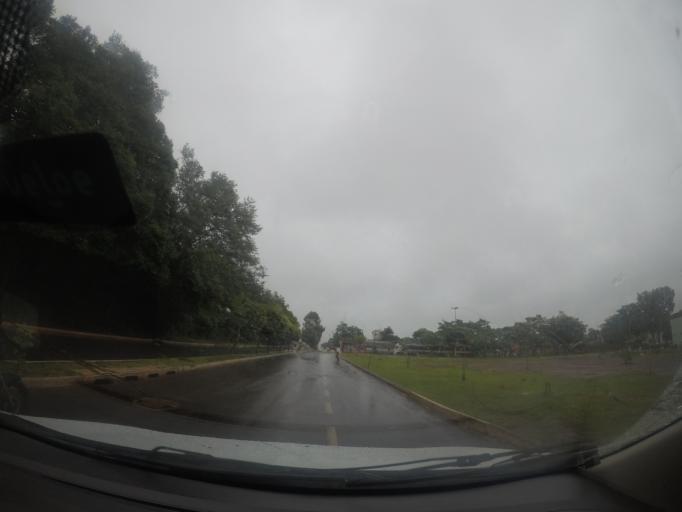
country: BR
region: Goias
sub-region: Goiania
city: Goiania
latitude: -16.6024
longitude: -49.3412
